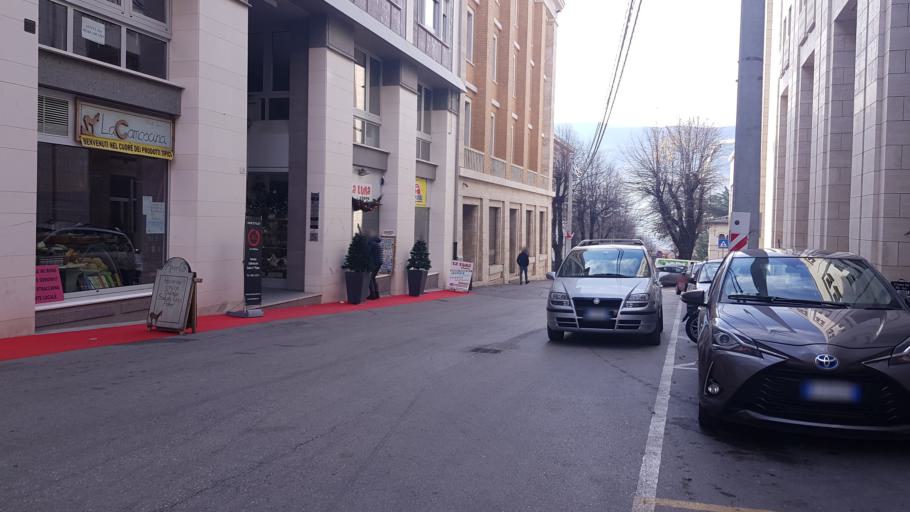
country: IT
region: Abruzzo
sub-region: Provincia dell' Aquila
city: L'Aquila
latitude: 42.3469
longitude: 13.3979
